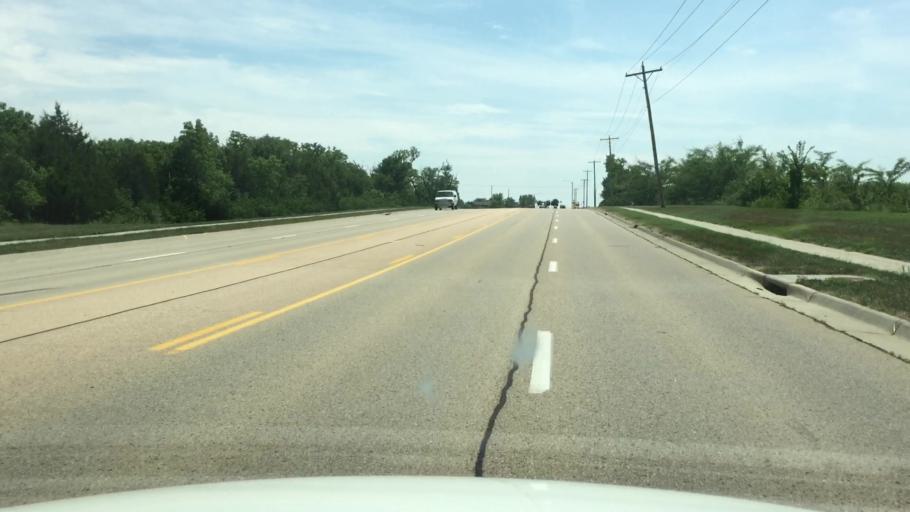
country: US
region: Kansas
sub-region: Shawnee County
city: Topeka
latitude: 38.9899
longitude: -95.6145
